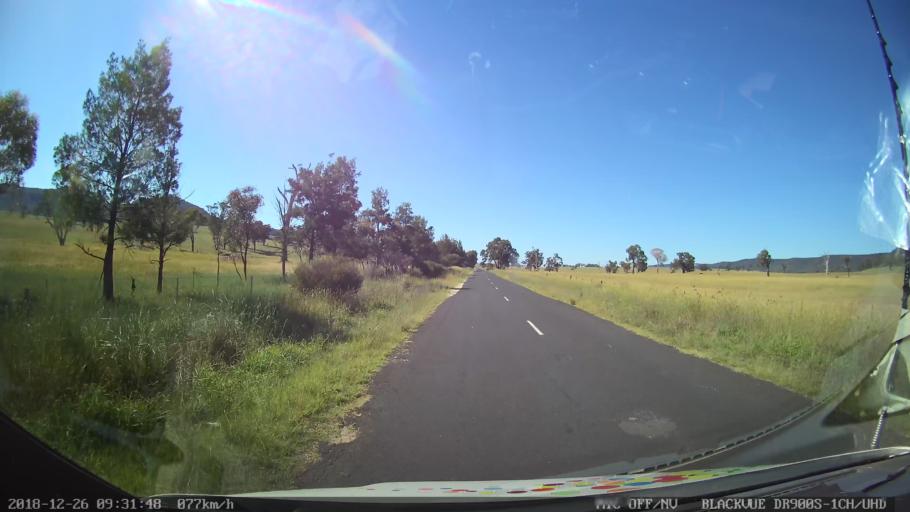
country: AU
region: New South Wales
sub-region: Mid-Western Regional
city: Kandos
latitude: -32.8768
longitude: 150.0320
